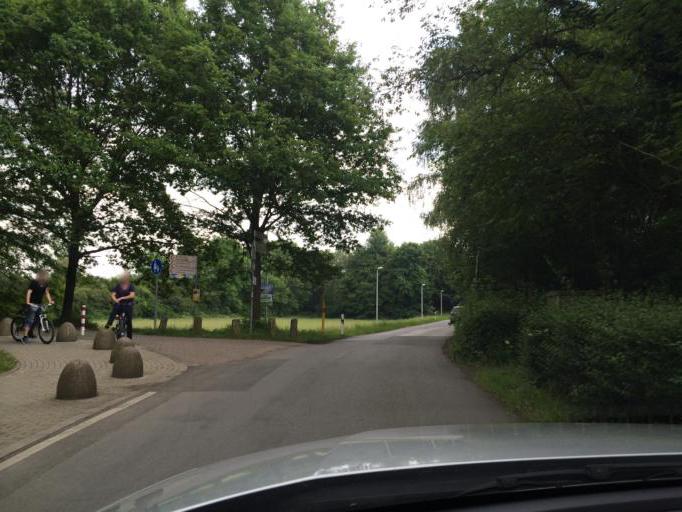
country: DE
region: North Rhine-Westphalia
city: Witten
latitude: 51.4299
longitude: 7.3150
